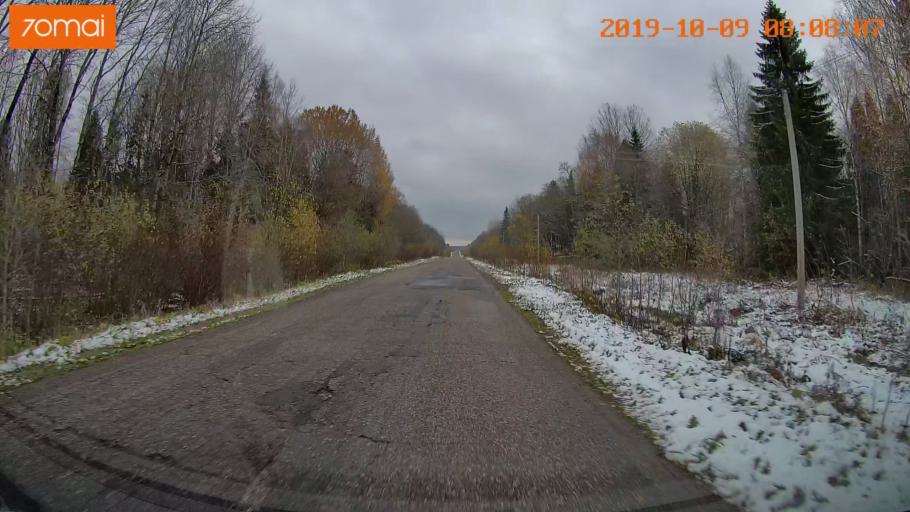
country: RU
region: Jaroslavl
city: Kukoboy
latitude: 58.7022
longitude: 40.0907
